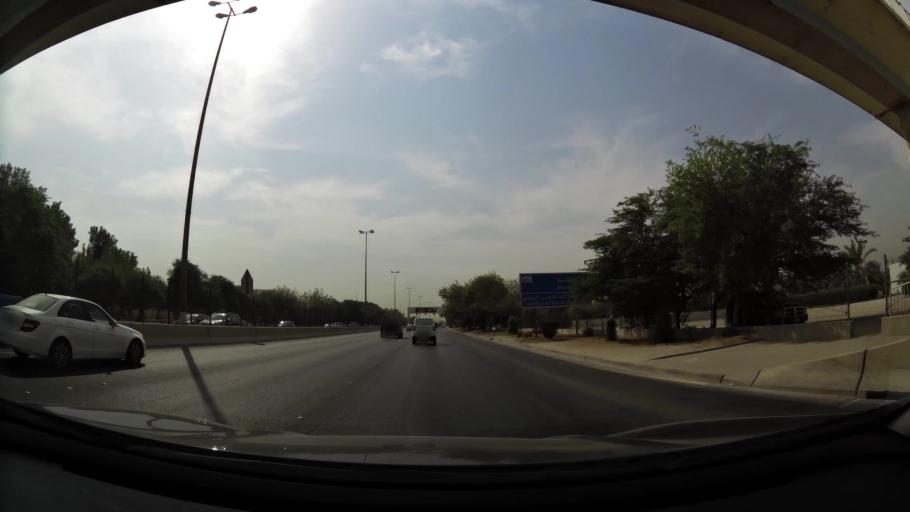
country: KW
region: Al Asimah
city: Ash Shamiyah
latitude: 29.3501
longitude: 47.9728
